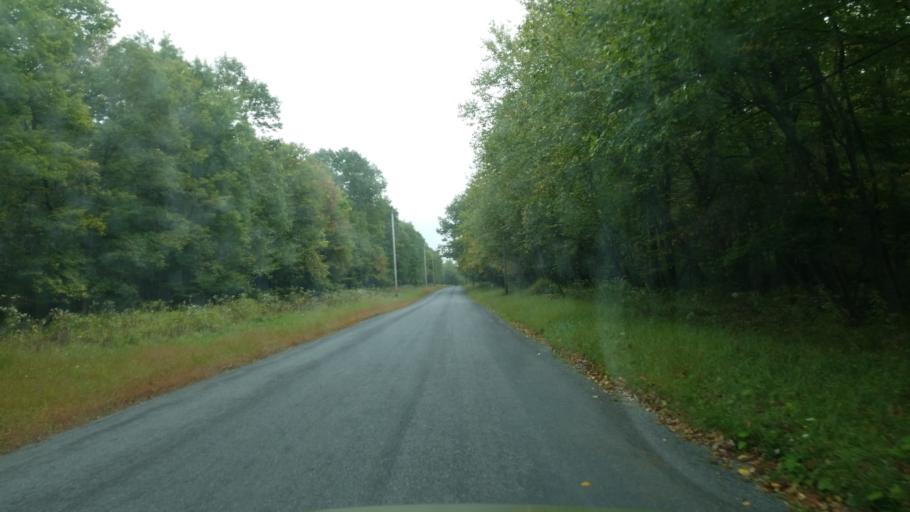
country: US
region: Pennsylvania
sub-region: Clearfield County
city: Curwensville
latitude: 41.0360
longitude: -78.5622
